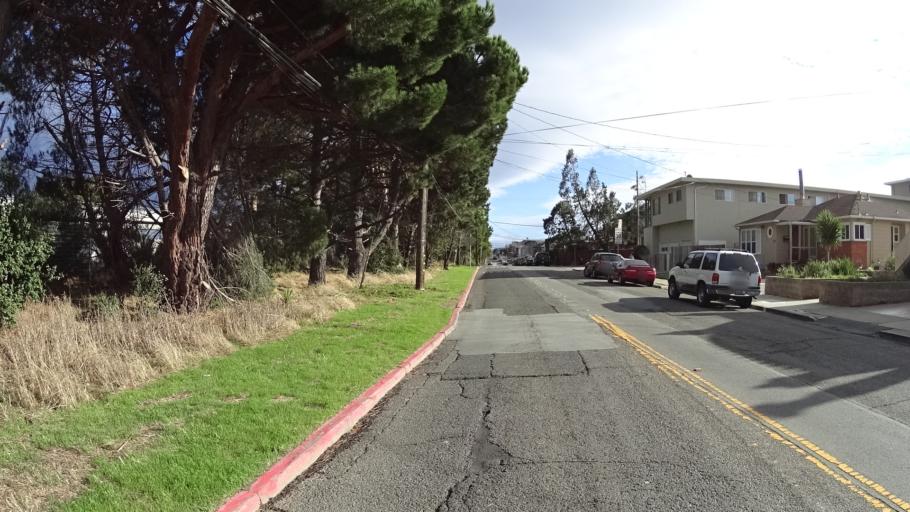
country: US
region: California
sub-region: San Mateo County
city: San Bruno
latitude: 37.6192
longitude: -122.4050
